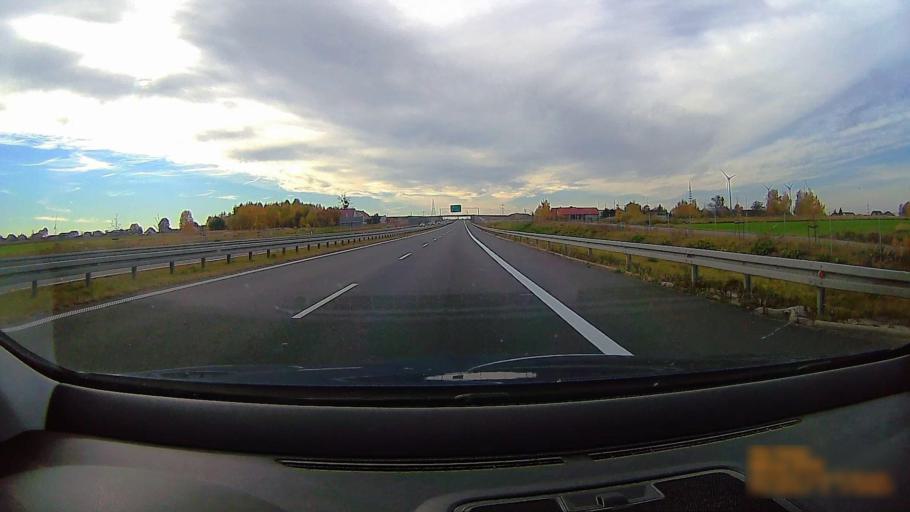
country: PL
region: Greater Poland Voivodeship
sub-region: Powiat ostrowski
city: Przygodzice
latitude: 51.6374
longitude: 17.8743
